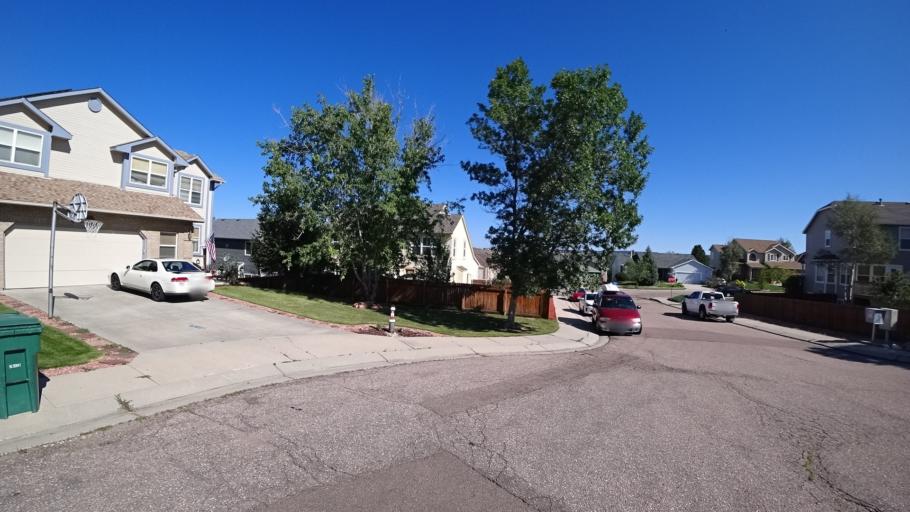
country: US
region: Colorado
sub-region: El Paso County
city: Gleneagle
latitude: 38.9806
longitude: -104.7801
